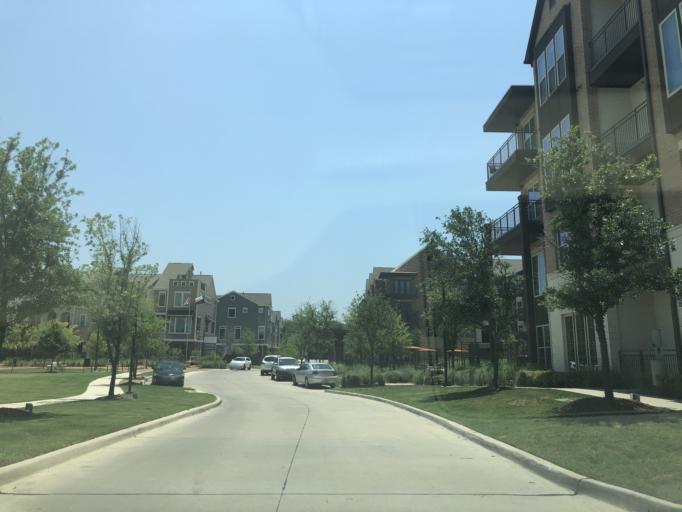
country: US
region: Texas
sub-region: Dallas County
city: Dallas
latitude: 32.7780
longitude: -96.8409
